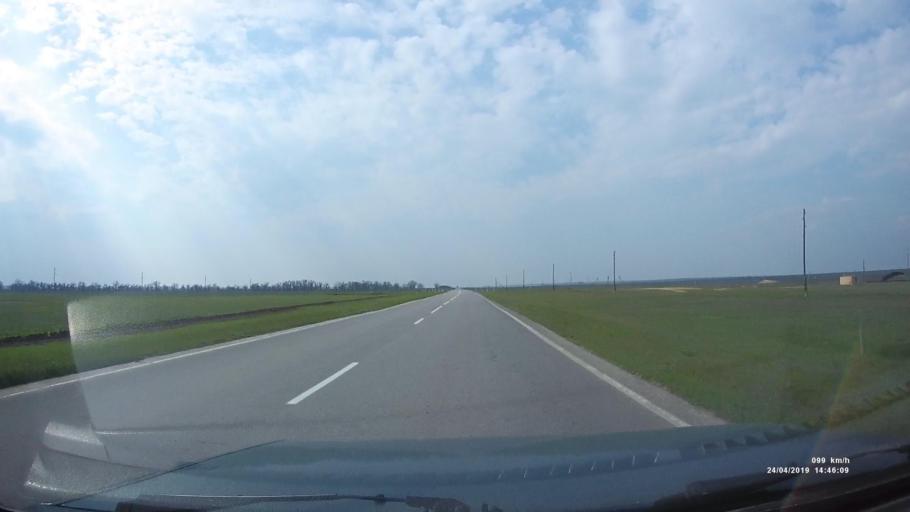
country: RU
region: Rostov
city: Remontnoye
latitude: 46.4794
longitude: 43.7950
